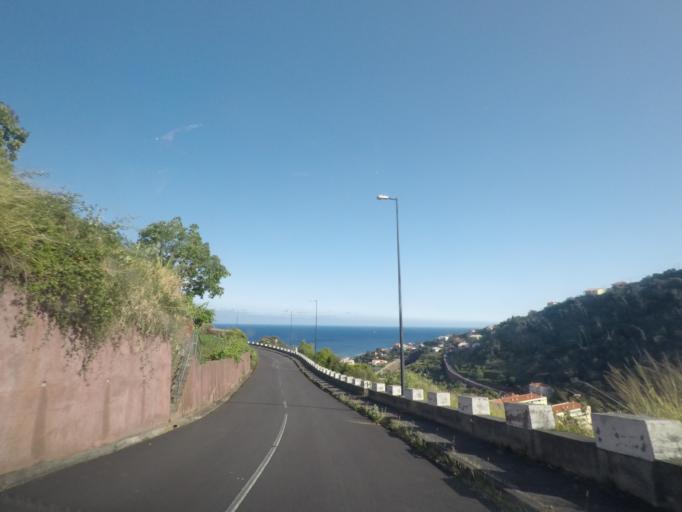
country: PT
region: Madeira
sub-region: Santa Cruz
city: Santa Cruz
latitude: 32.6922
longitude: -16.7964
